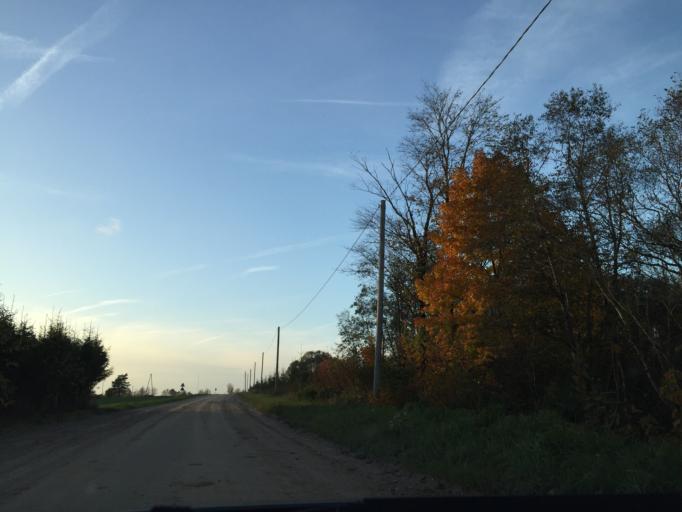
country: LV
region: Malpils
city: Malpils
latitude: 56.8836
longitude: 24.9660
